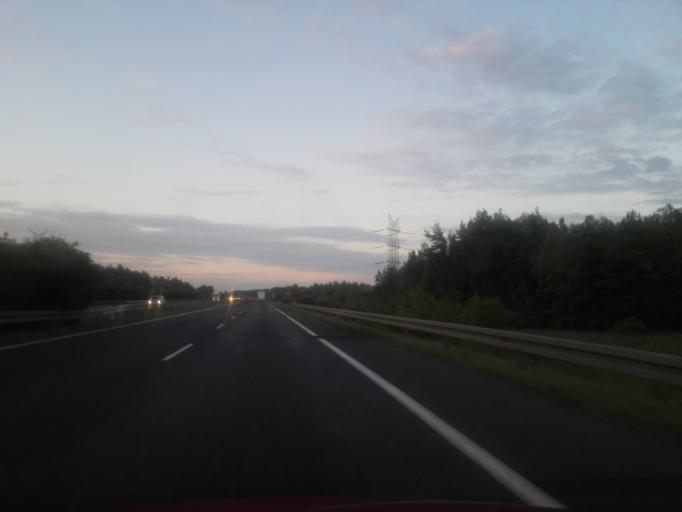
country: PL
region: Silesian Voivodeship
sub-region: Powiat czestochowski
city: Borowno
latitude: 51.0281
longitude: 19.3279
